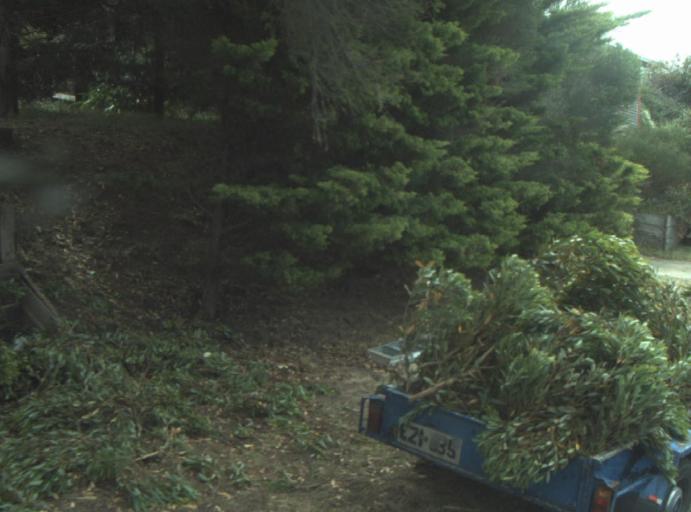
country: AU
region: Victoria
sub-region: Greater Geelong
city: Leopold
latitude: -38.2644
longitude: 144.5451
